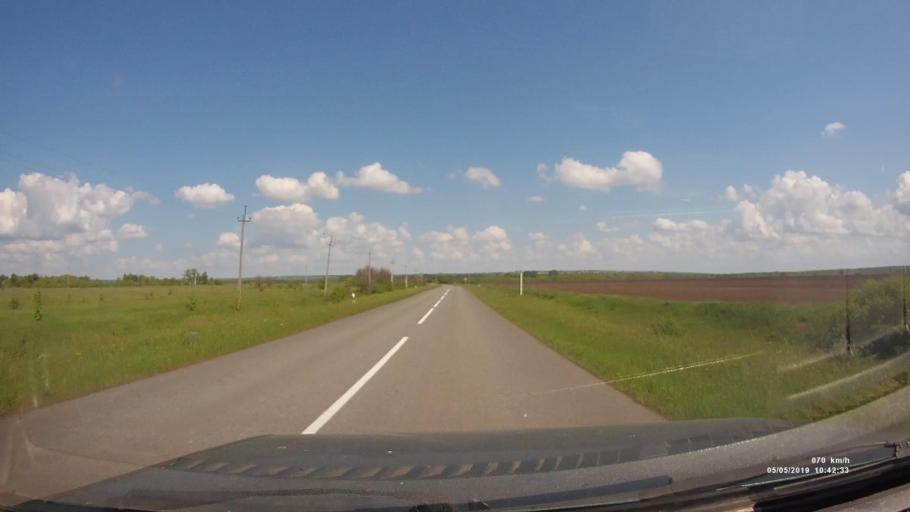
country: RU
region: Rostov
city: Ust'-Donetskiy
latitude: 47.6005
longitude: 40.8385
